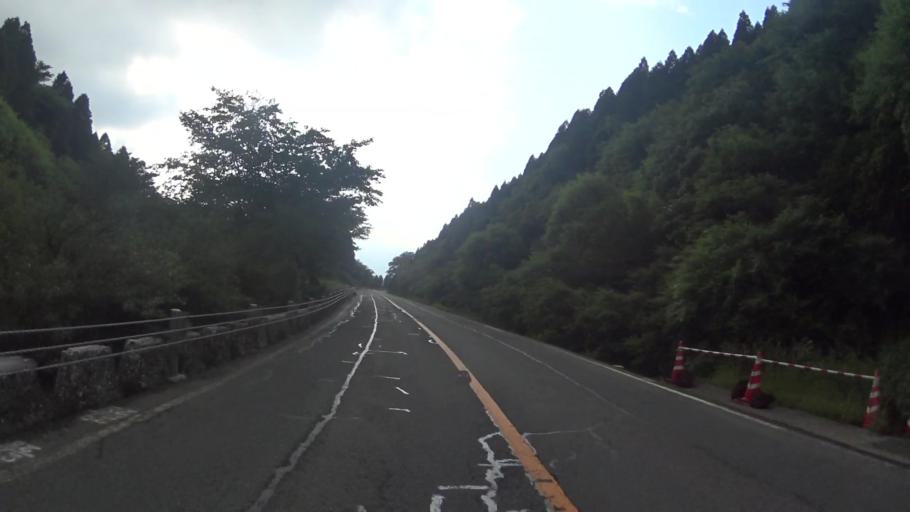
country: JP
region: Kumamoto
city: Aso
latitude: 32.8888
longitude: 131.0533
